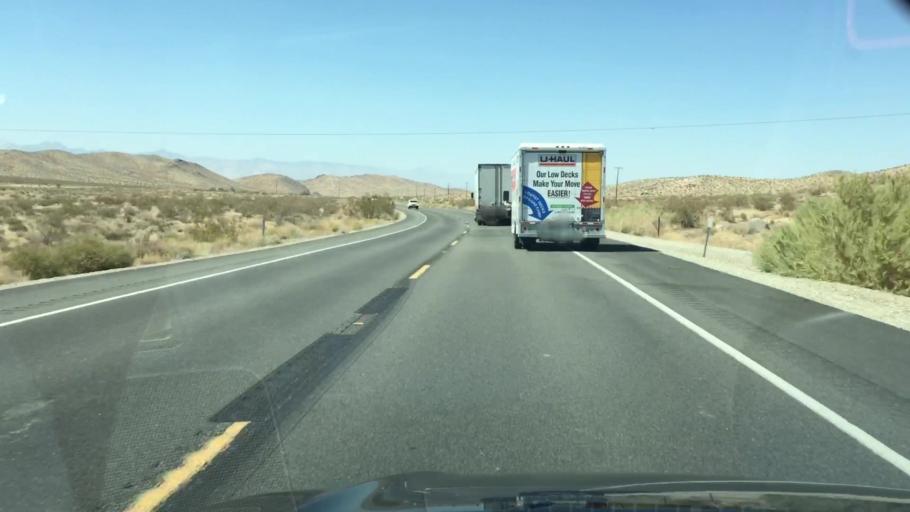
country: US
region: California
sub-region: Kern County
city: Ridgecrest
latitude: 35.5211
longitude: -117.6737
